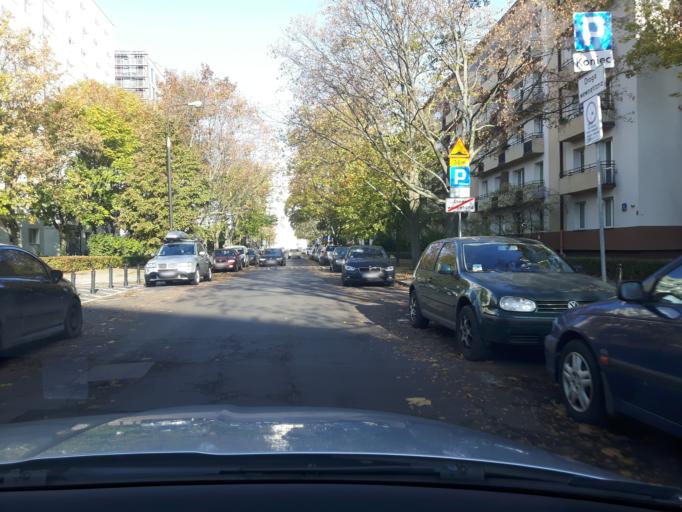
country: PL
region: Masovian Voivodeship
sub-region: Warszawa
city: Wola
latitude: 52.2519
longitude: 20.9930
